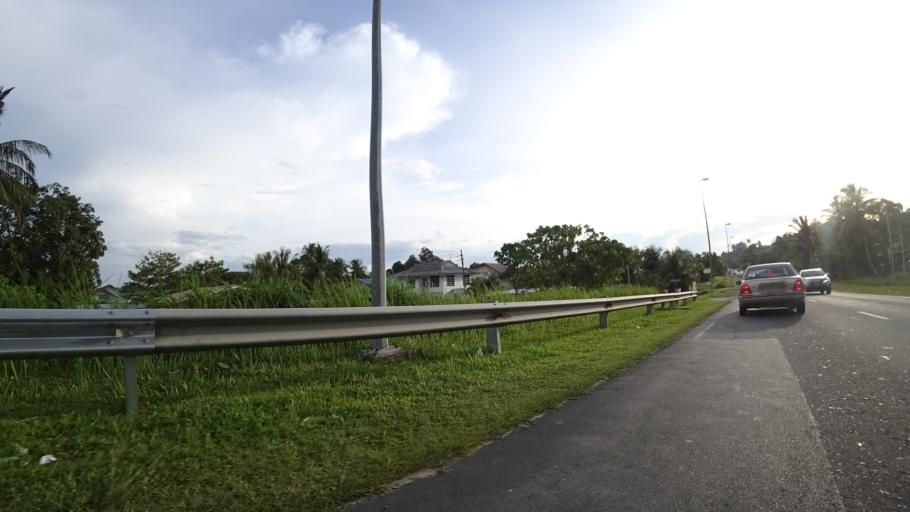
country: BN
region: Brunei and Muara
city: Bandar Seri Begawan
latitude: 4.8837
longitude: 114.8359
